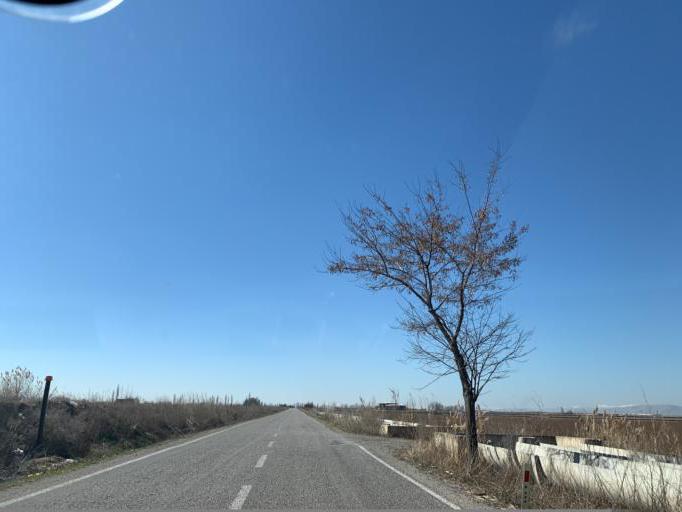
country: TR
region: Konya
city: Cumra
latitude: 37.6189
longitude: 32.8004
